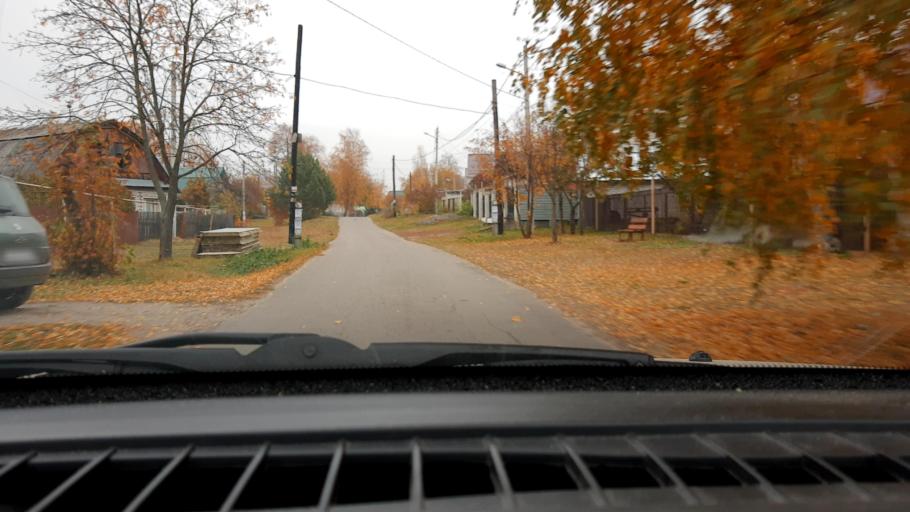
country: RU
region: Nizjnij Novgorod
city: Gorbatovka
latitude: 56.2104
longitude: 43.7589
